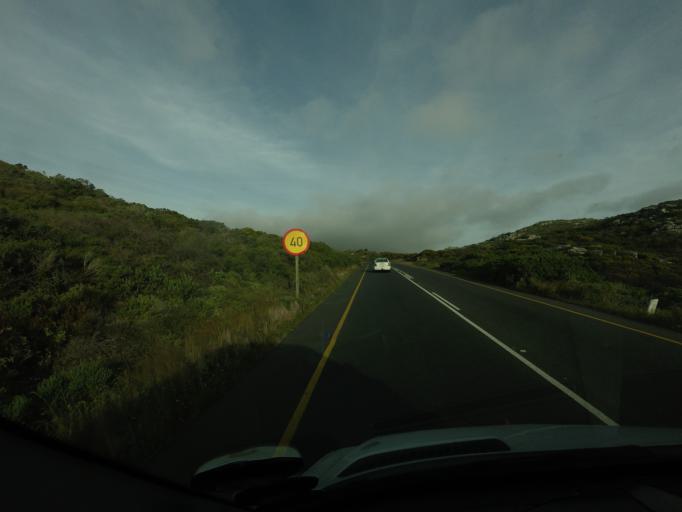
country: ZA
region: Western Cape
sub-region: City of Cape Town
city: Constantia
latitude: -34.1129
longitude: 18.3978
